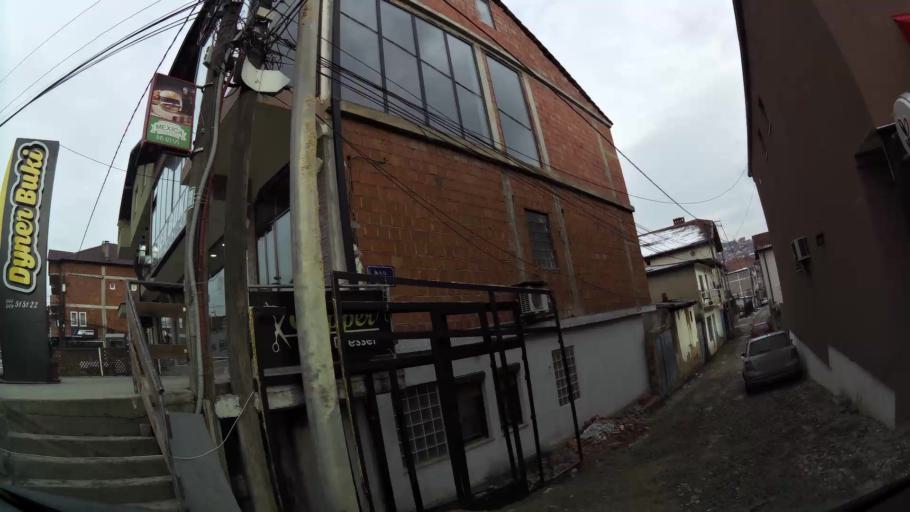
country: XK
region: Pristina
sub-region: Komuna e Prishtines
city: Pristina
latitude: 42.6747
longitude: 21.1683
